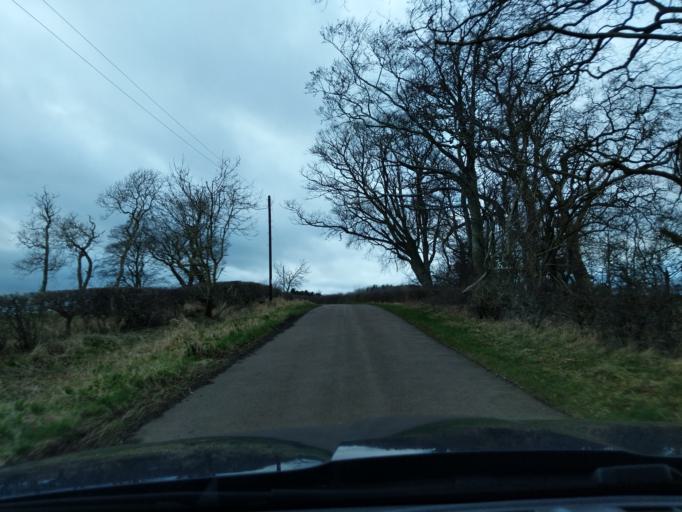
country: GB
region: England
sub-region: Northumberland
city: Ancroft
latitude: 55.7112
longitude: -2.0338
